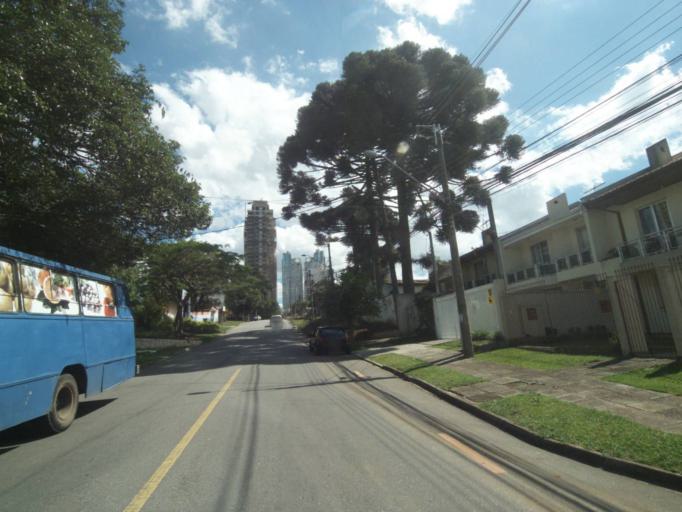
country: BR
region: Parana
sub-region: Curitiba
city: Curitiba
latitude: -25.4356
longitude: -49.3355
